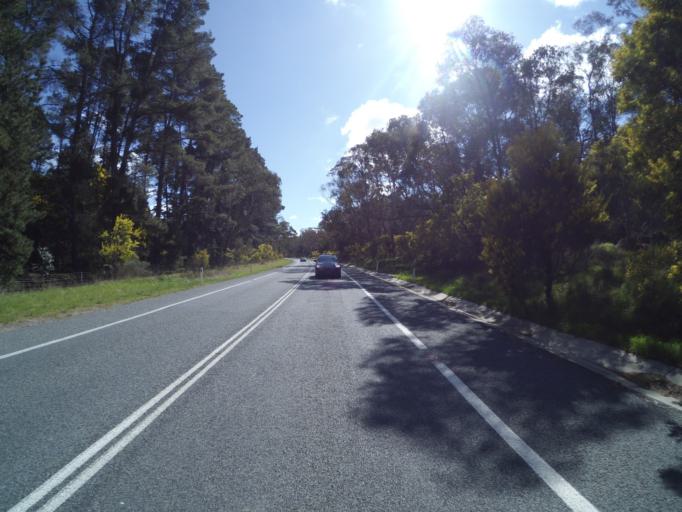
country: AU
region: New South Wales
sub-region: Queanbeyan
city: Queanbeyan
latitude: -35.2838
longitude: 149.2595
